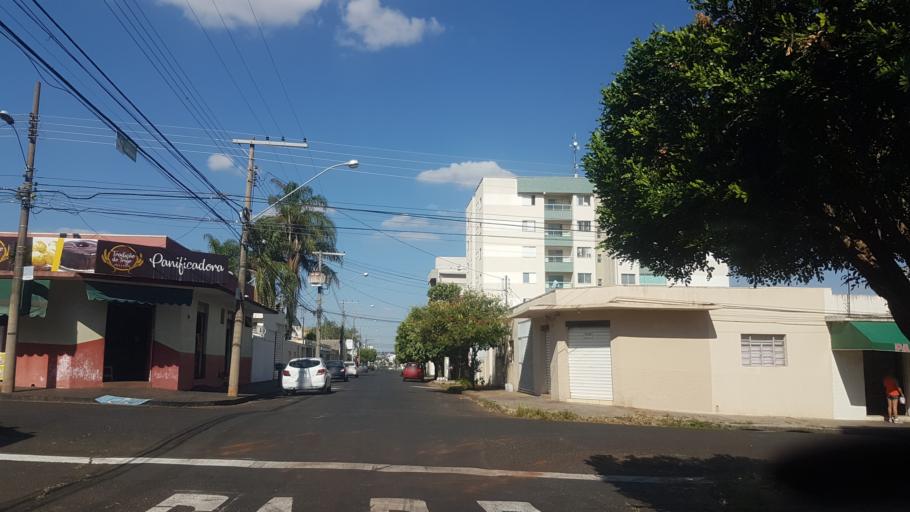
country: BR
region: Minas Gerais
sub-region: Uberlandia
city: Uberlandia
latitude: -18.8947
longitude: -48.2659
